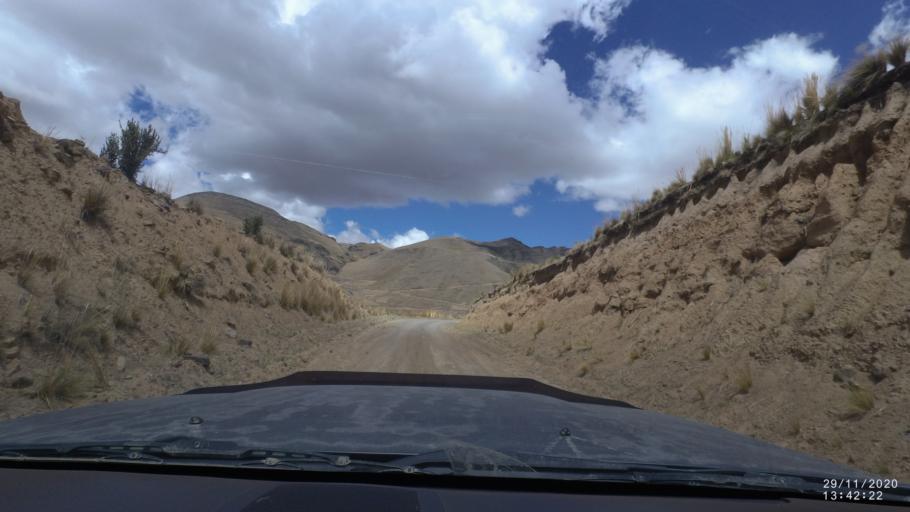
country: BO
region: Cochabamba
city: Cochabamba
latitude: -17.1363
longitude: -66.3238
